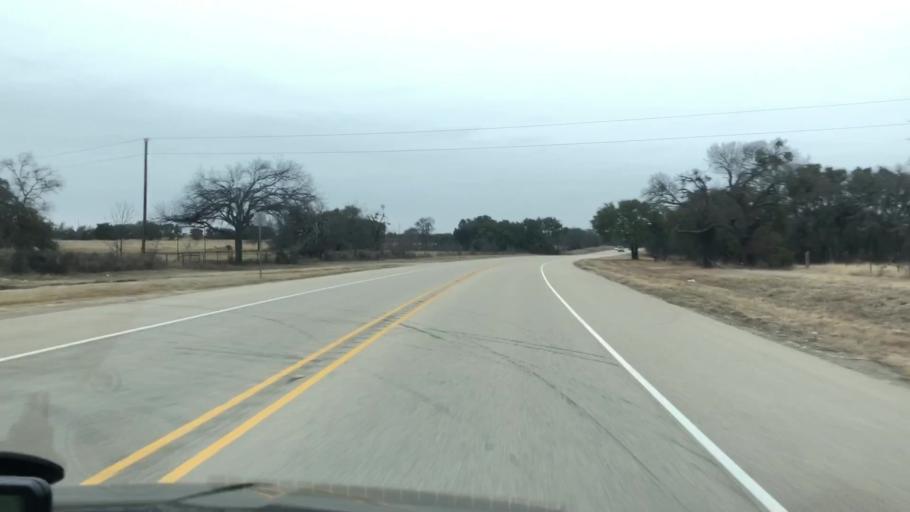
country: US
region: Texas
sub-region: Hamilton County
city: Hamilton
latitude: 31.5476
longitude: -98.1601
